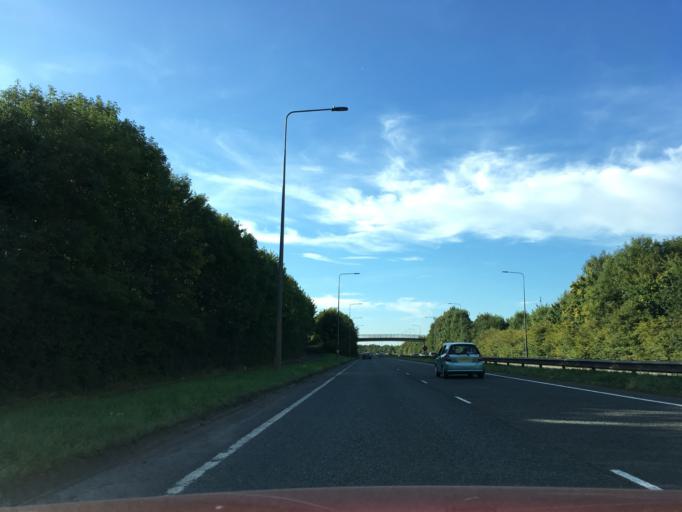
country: GB
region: England
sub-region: South Gloucestershire
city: Mangotsfield
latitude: 51.5015
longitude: -2.4833
